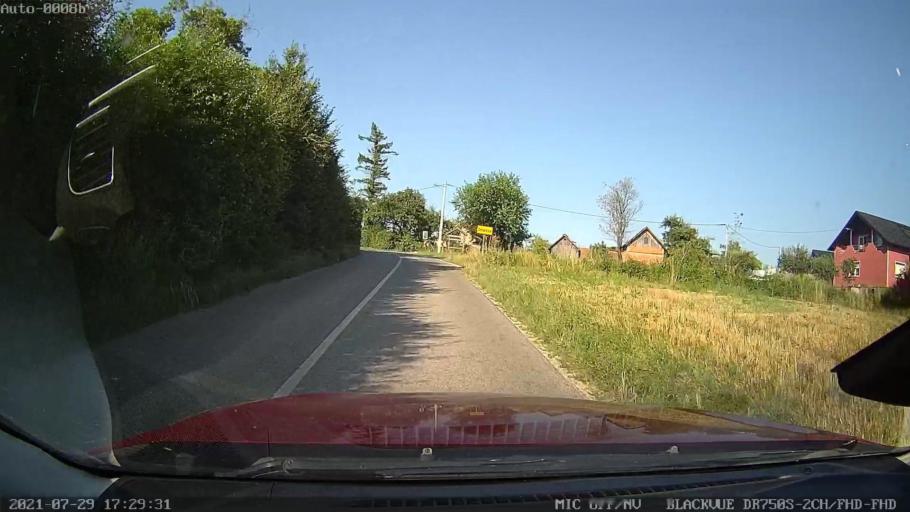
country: HR
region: Varazdinska
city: Klenovnik
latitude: 46.2734
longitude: 16.1198
